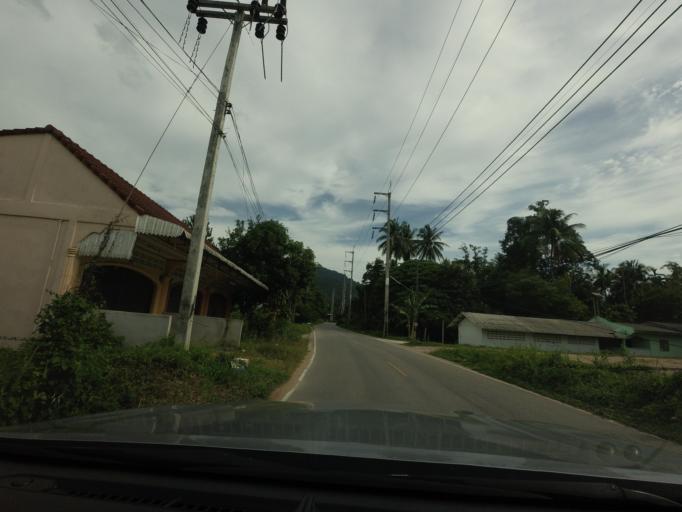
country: TH
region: Yala
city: Yala
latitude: 6.5039
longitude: 101.2870
